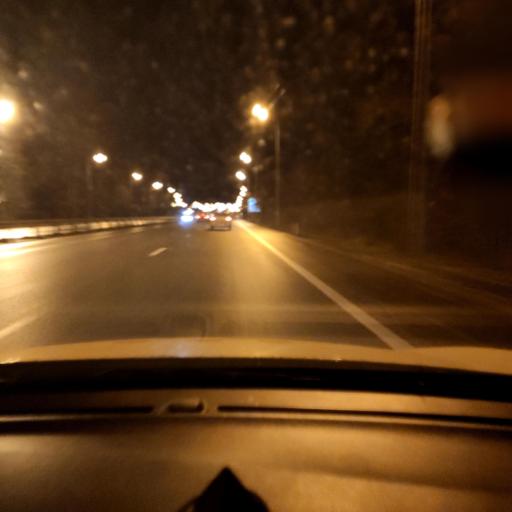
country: RU
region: Tatarstan
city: Osinovo
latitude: 55.8504
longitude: 48.8535
